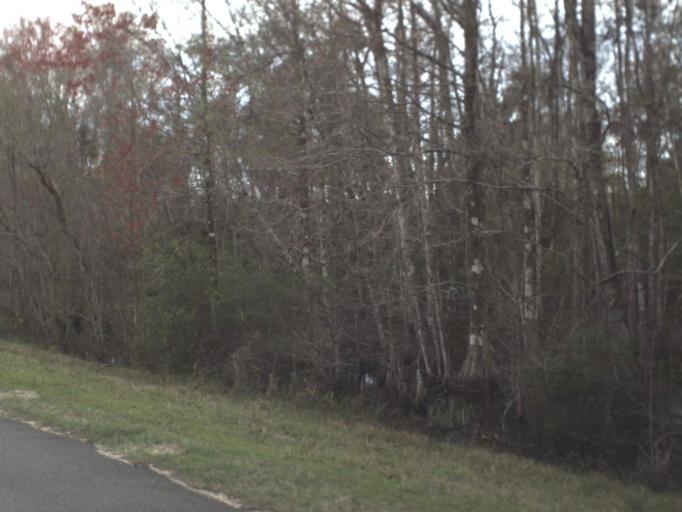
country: US
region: Florida
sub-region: Leon County
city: Woodville
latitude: 30.1755
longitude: -84.0096
